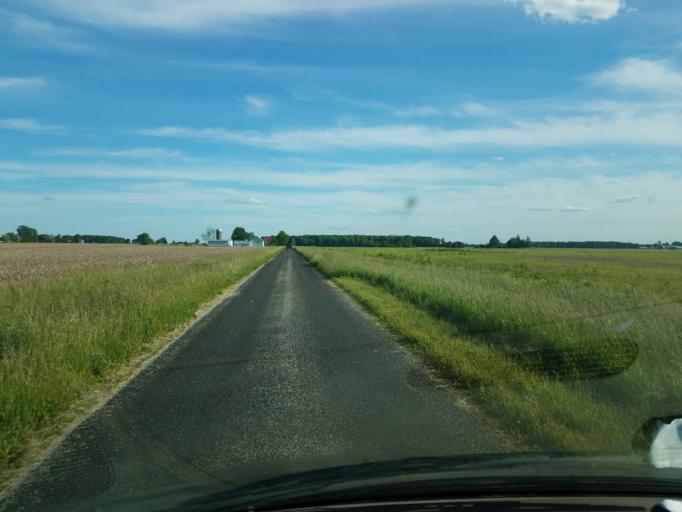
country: US
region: Ohio
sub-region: Morrow County
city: Cardington
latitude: 40.5209
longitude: -82.9862
